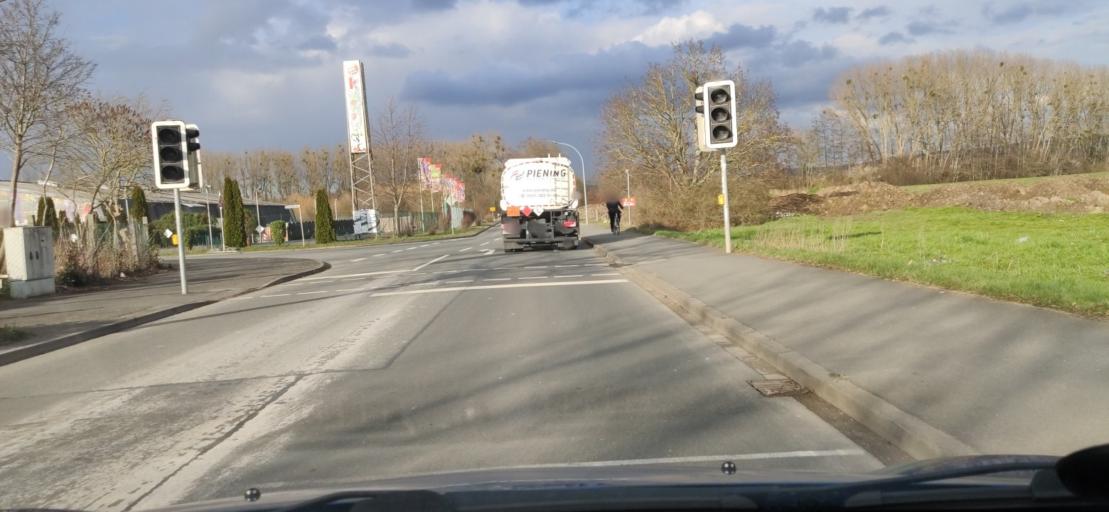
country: DE
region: Lower Saxony
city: Rosdorf
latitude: 51.5100
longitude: 9.9150
